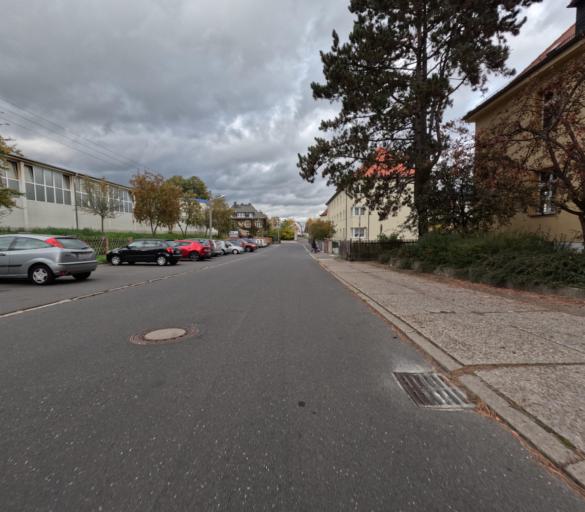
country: DE
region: Saxony
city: Grimma
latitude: 51.2324
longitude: 12.7163
